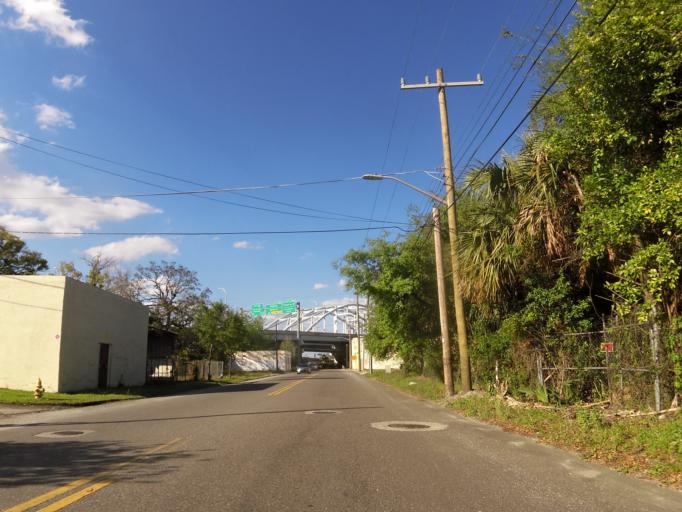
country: US
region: Florida
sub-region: Duval County
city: Jacksonville
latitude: 30.3267
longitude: -81.6774
